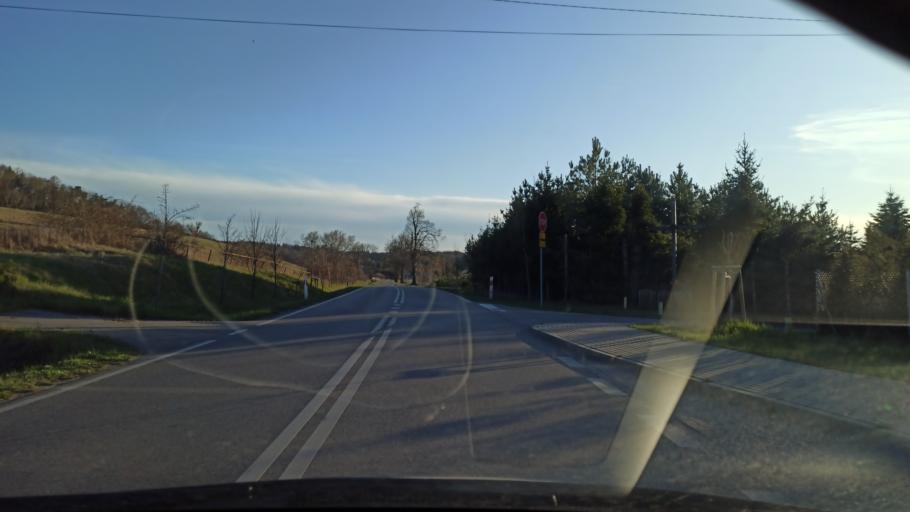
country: PL
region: Warmian-Masurian Voivodeship
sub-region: Powiat elblaski
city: Tolkmicko
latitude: 54.3070
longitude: 19.5123
